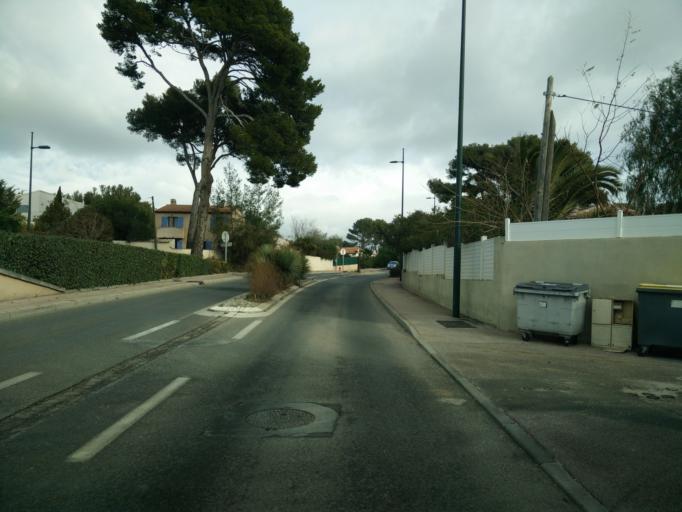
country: FR
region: Provence-Alpes-Cote d'Azur
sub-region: Departement du Var
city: Six-Fours-les-Plages
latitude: 43.0776
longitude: 5.8166
